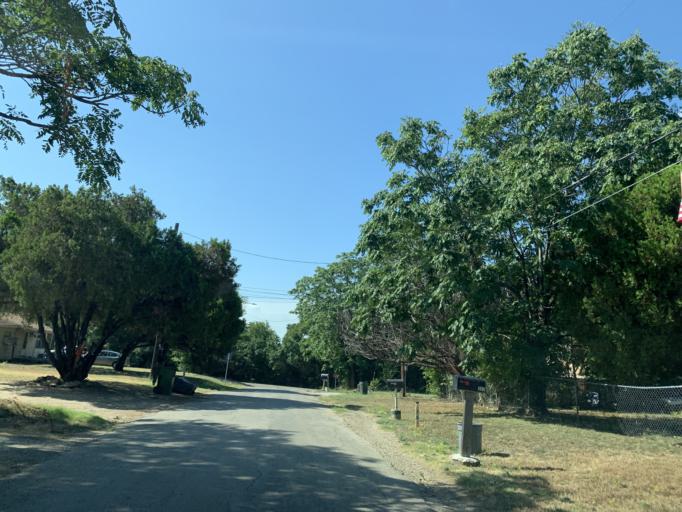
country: US
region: Texas
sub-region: Tarrant County
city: Azle
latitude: 32.8612
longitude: -97.5179
